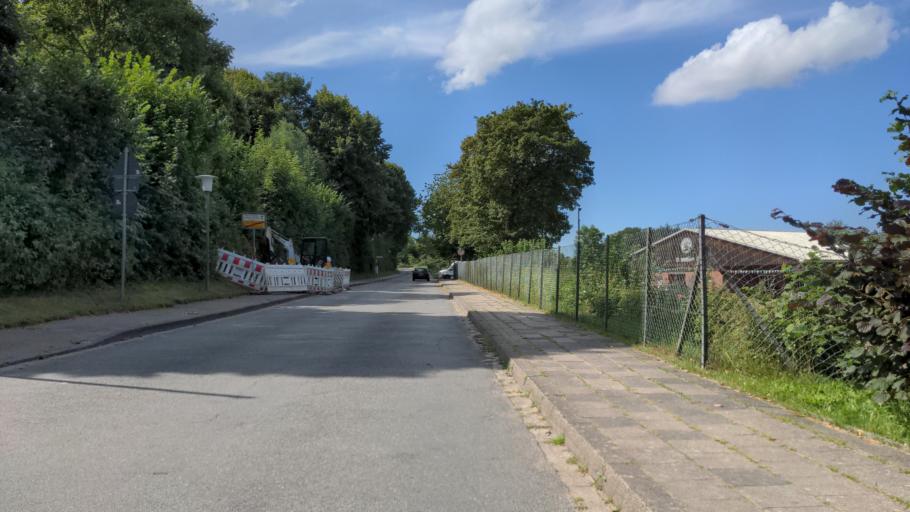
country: DE
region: Schleswig-Holstein
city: Malente
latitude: 54.1781
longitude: 10.5538
